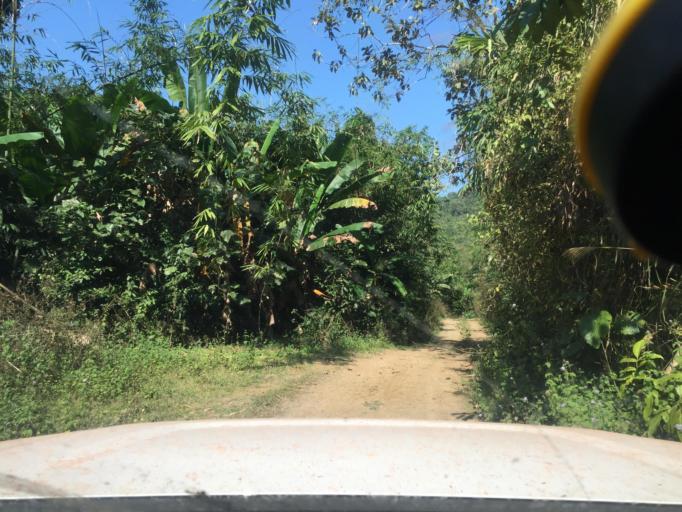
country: LA
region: Phongsali
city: Phongsali
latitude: 21.7010
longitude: 102.3942
